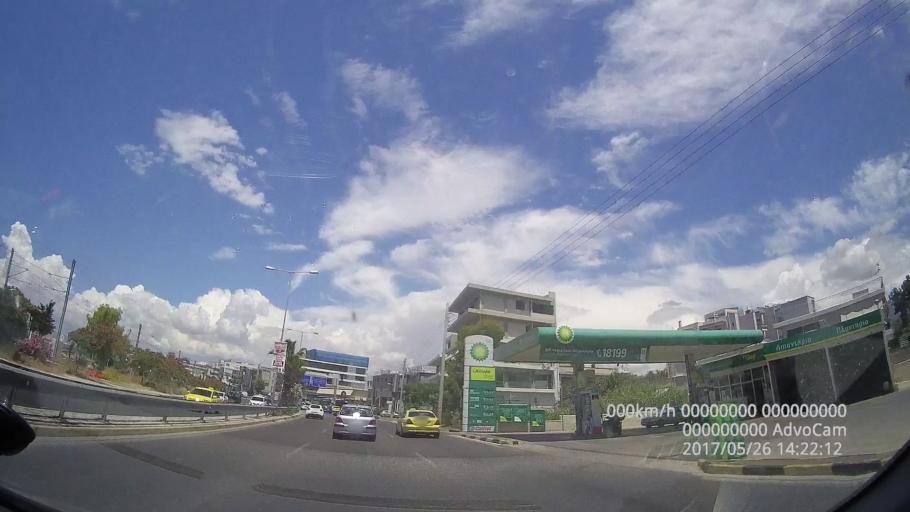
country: GR
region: Attica
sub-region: Nomarchia Athinas
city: Agioi Anargyroi
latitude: 38.0124
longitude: 23.7186
